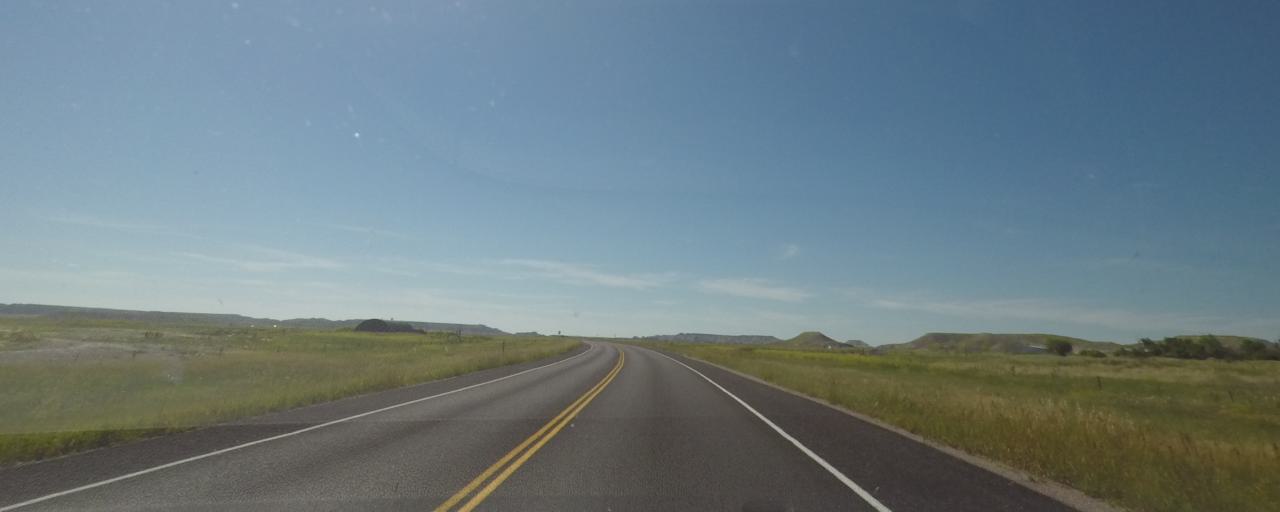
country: US
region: South Dakota
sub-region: Shannon County
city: Porcupine
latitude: 43.7823
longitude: -102.5526
